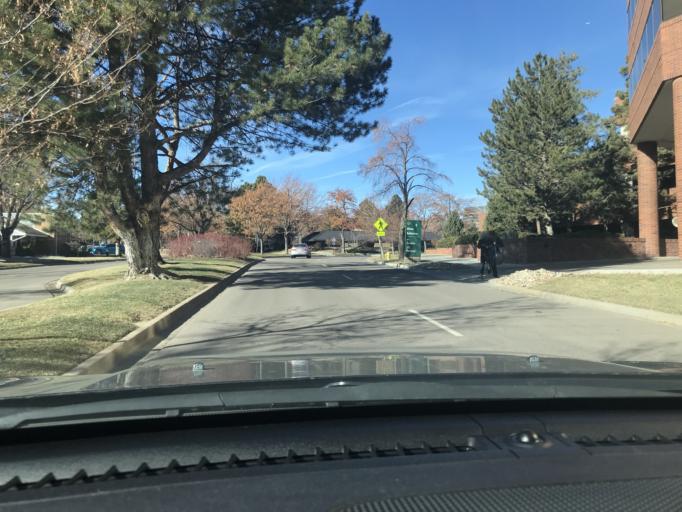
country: US
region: Colorado
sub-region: Arapahoe County
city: Castlewood
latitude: 39.6205
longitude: -104.8937
